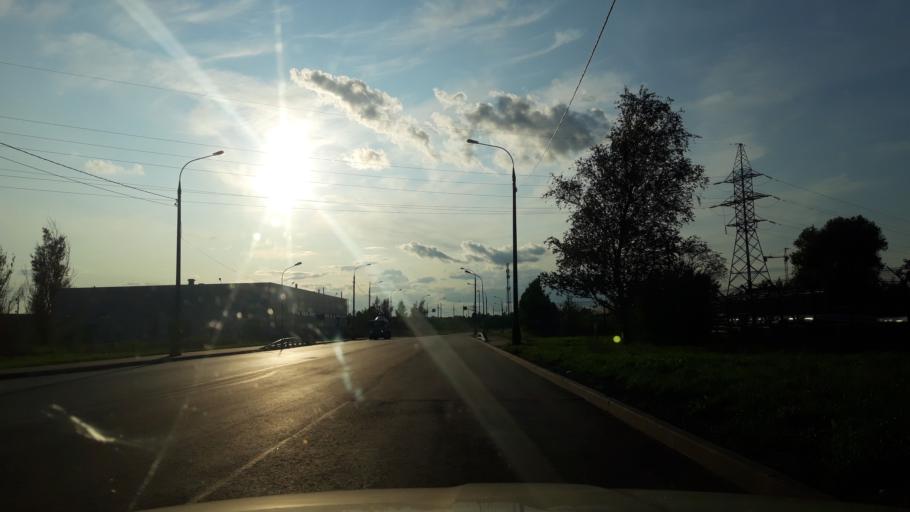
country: RU
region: Moskovskaya
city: Alabushevo
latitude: 56.0020
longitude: 37.1524
